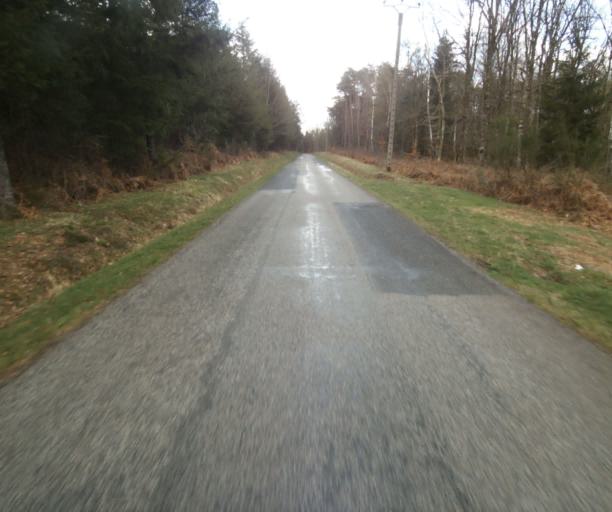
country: FR
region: Limousin
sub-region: Departement de la Correze
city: Correze
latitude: 45.2504
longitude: 1.9289
